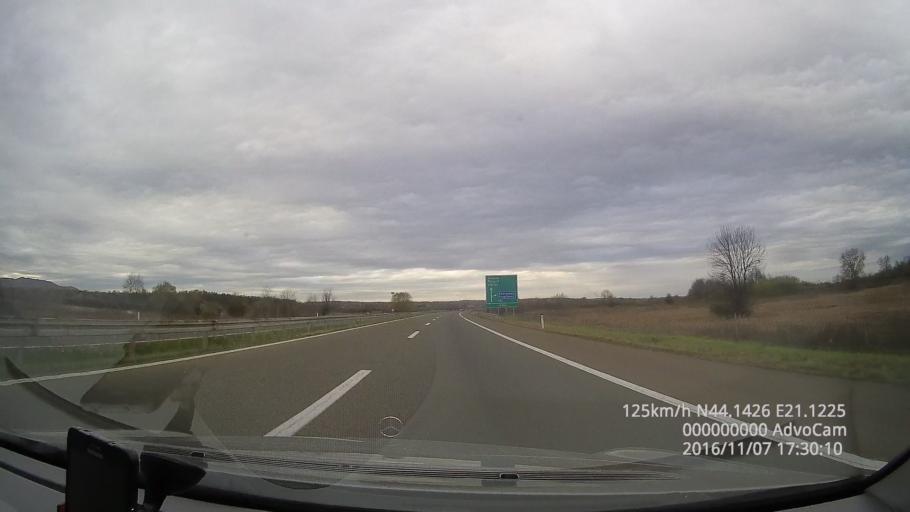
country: RS
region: Central Serbia
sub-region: Sumadijski Okrug
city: Batocina
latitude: 44.1426
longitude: 21.1226
